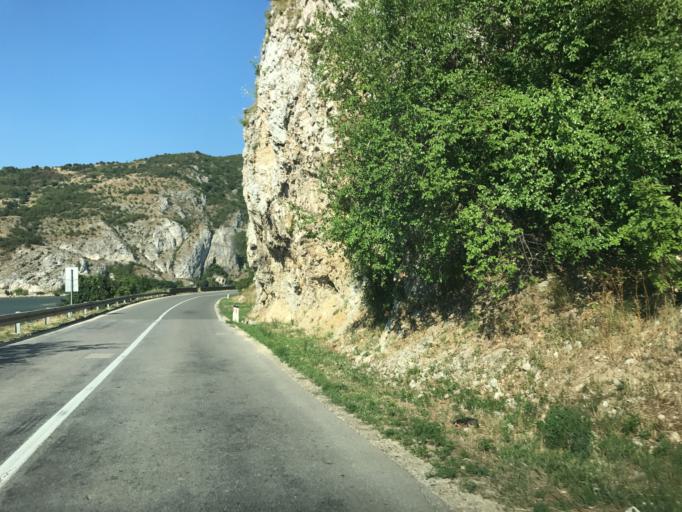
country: RO
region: Caras-Severin
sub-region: Comuna Pescari
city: Coronini
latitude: 44.6609
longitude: 21.6924
